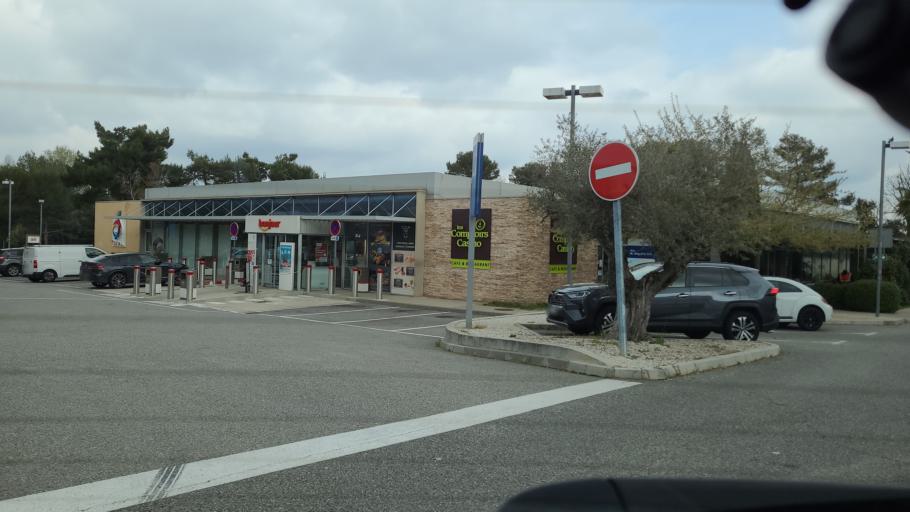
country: FR
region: Provence-Alpes-Cote d'Azur
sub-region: Departement des Alpes-Maritimes
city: Le Cannet
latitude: 43.5892
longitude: 7.0353
